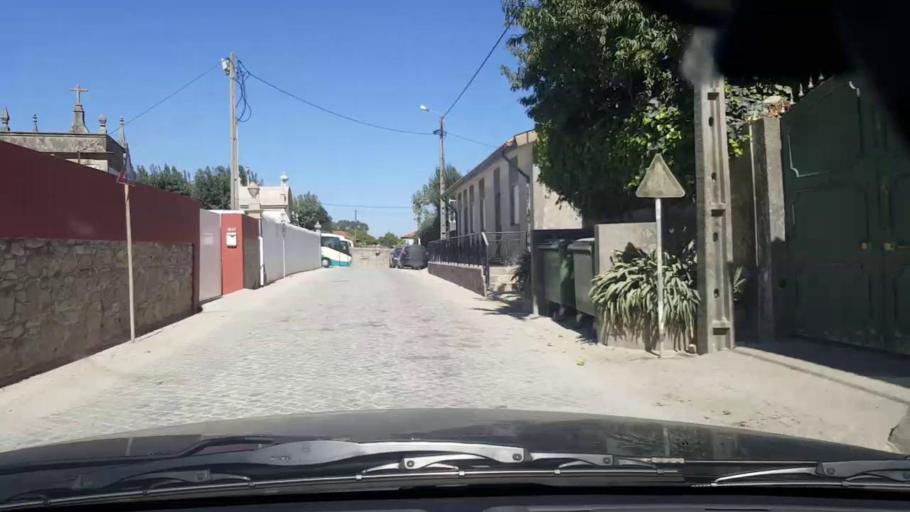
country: PT
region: Porto
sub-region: Maia
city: Gemunde
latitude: 41.3350
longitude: -8.6459
